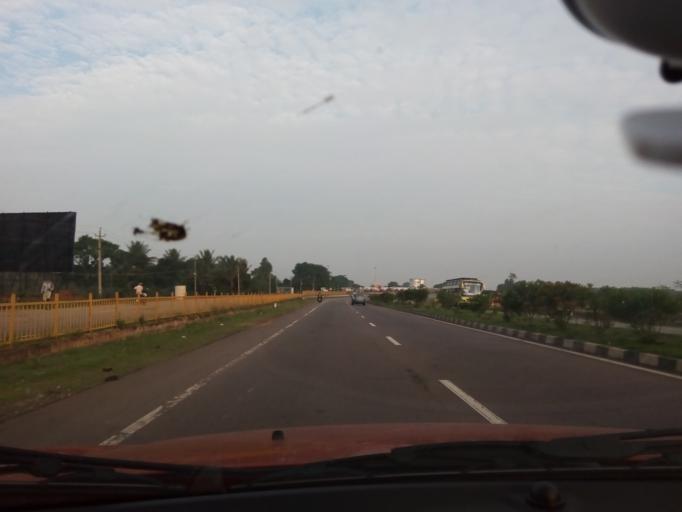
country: IN
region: Karnataka
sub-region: Ramanagara
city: Magadi
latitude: 13.0690
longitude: 77.2399
